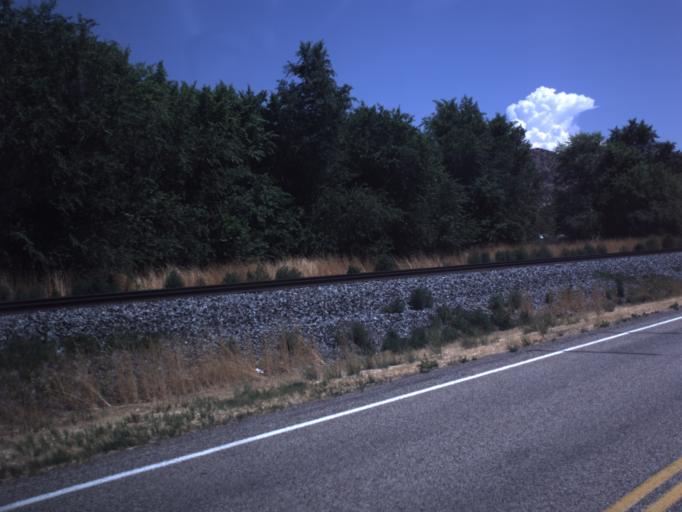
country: US
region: Utah
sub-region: Millard County
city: Delta
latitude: 39.5352
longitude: -112.2808
